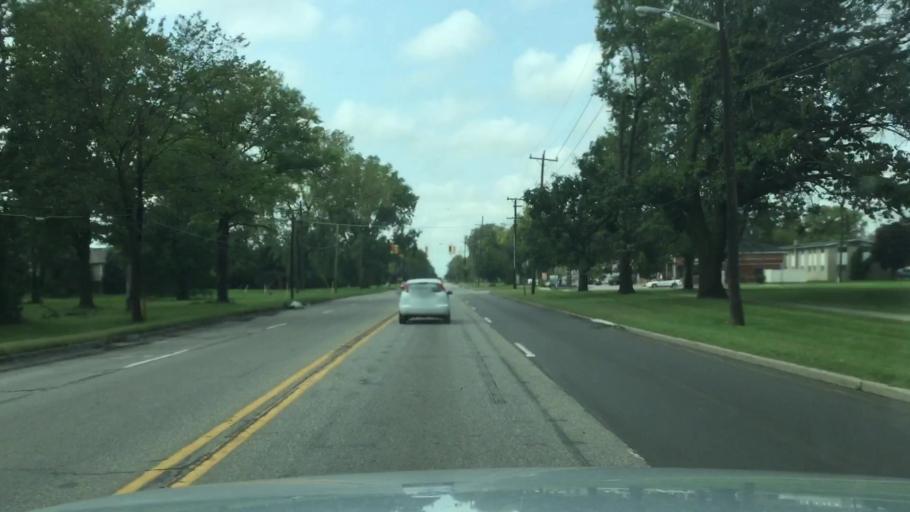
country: US
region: Michigan
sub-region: Wayne County
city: Wayne
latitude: 42.2670
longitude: -83.3708
